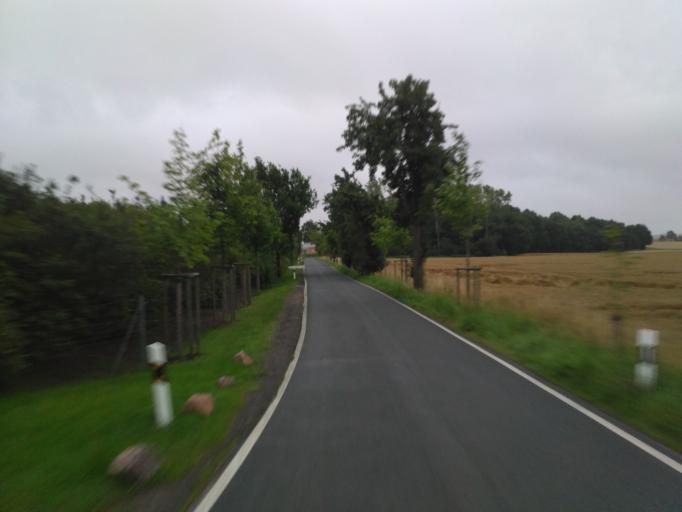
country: DE
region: Saxony
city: Nossen
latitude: 51.0854
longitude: 13.3626
